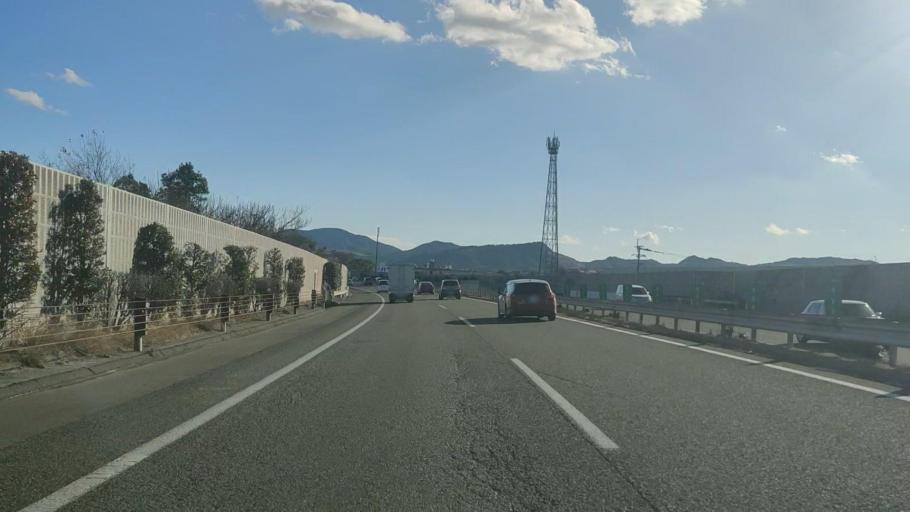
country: JP
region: Fukuoka
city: Umi
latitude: 33.5950
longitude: 130.4947
